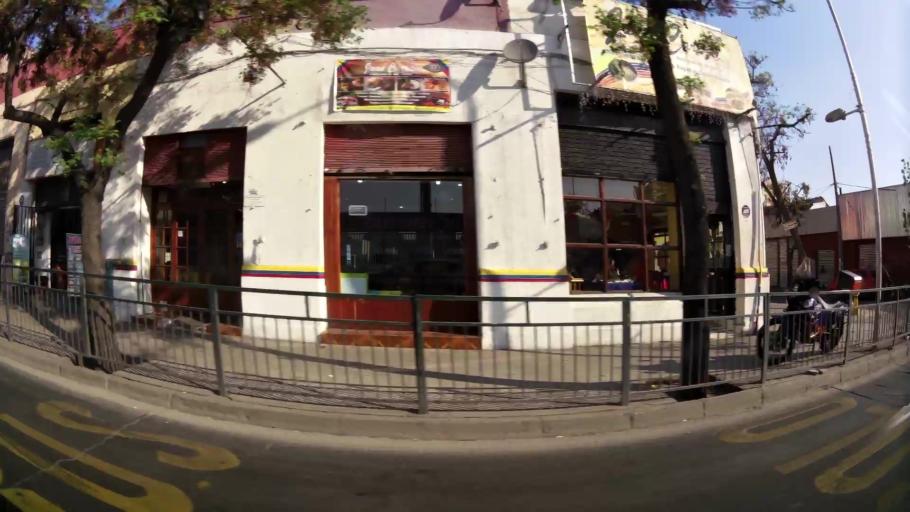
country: CL
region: Santiago Metropolitan
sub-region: Provincia de Santiago
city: Santiago
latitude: -33.4350
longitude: -70.6671
